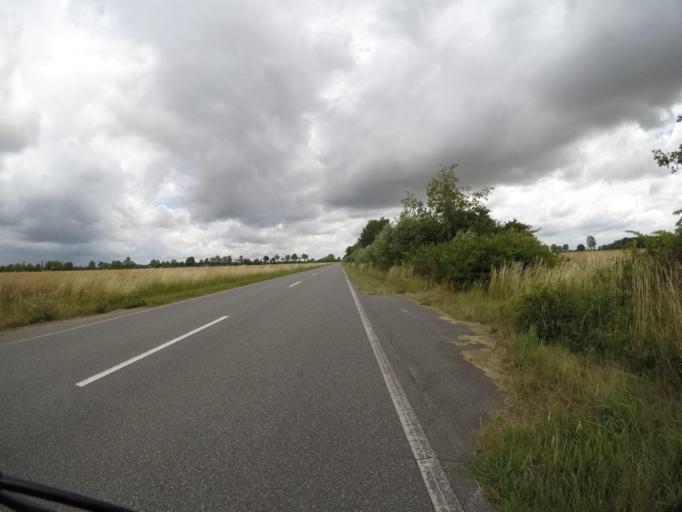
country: DE
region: Lower Saxony
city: Hitzacker
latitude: 53.1995
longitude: 11.1103
